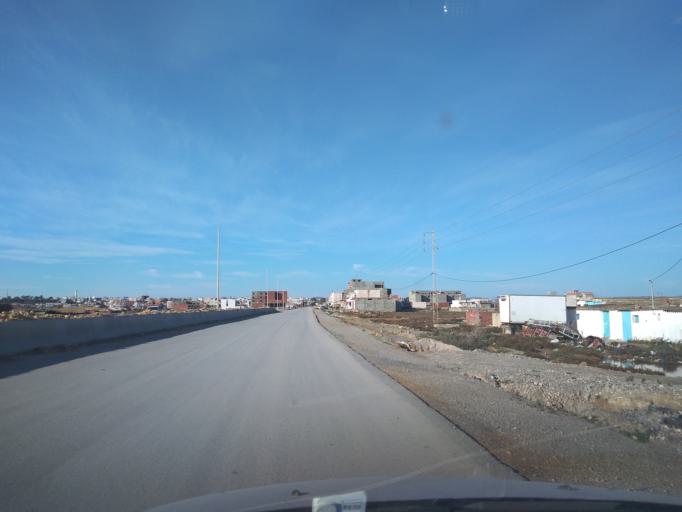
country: TN
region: Ariana
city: Qal'at al Andalus
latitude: 37.0478
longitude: 10.1247
